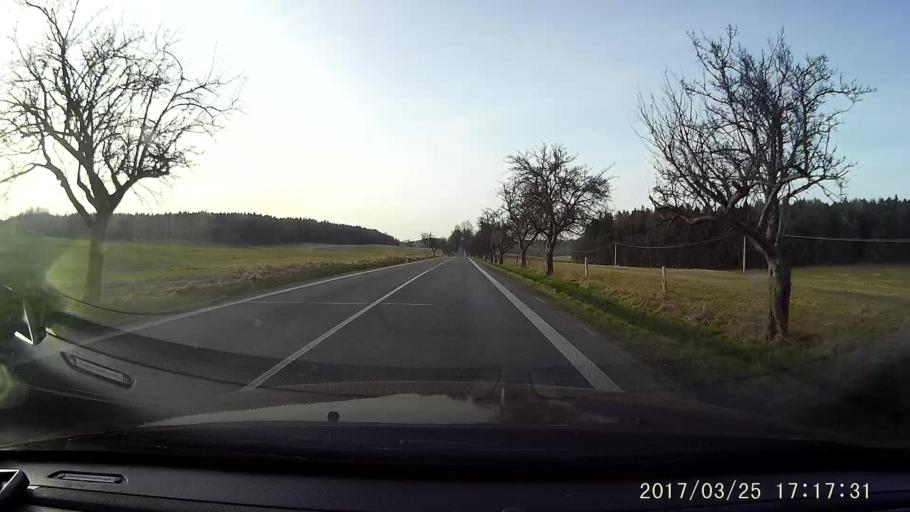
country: CZ
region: Liberecky
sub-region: Okres Liberec
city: Frydlant
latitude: 50.9674
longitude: 15.0962
